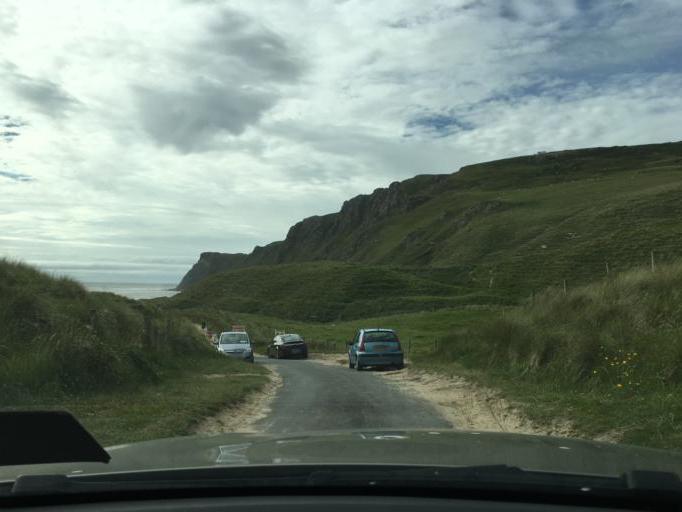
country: IE
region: Ulster
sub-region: County Donegal
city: Carndonagh
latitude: 55.3236
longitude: -7.3290
